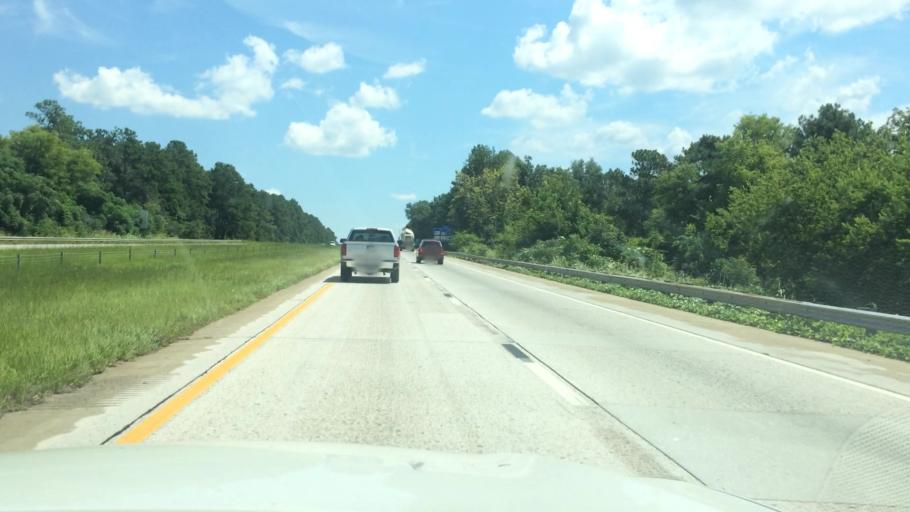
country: US
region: South Carolina
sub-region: Aiken County
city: Belvedere
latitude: 33.5557
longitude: -81.9472
